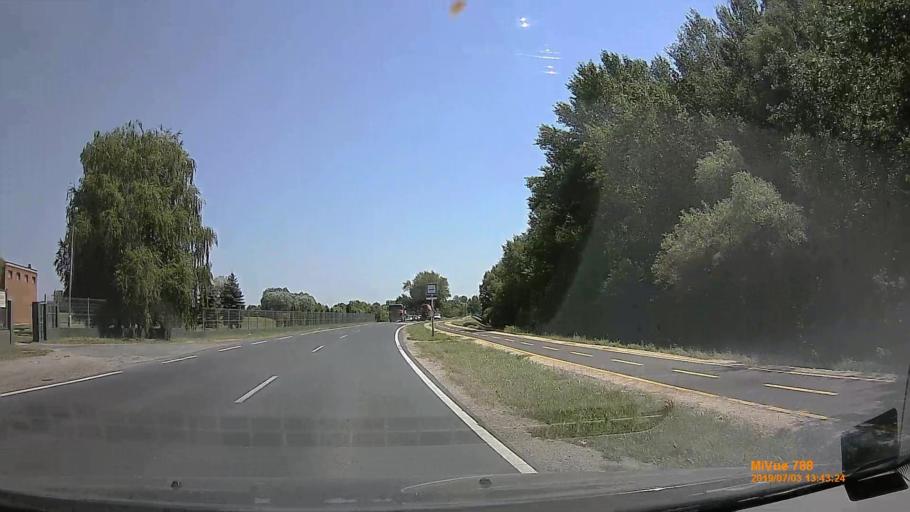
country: HU
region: Gyor-Moson-Sopron
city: Gyor
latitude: 47.7123
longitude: 17.6275
